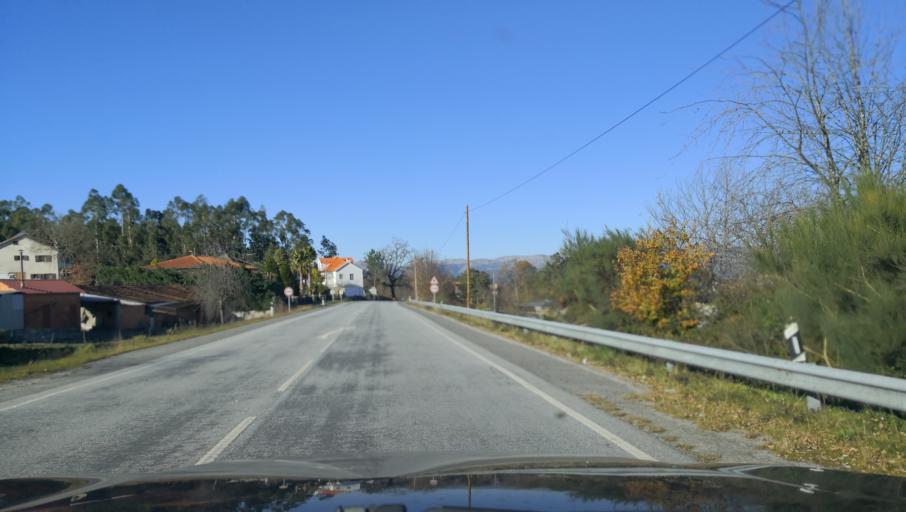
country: PT
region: Viseu
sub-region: Vouzela
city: Vouzela
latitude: 40.7052
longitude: -8.1432
